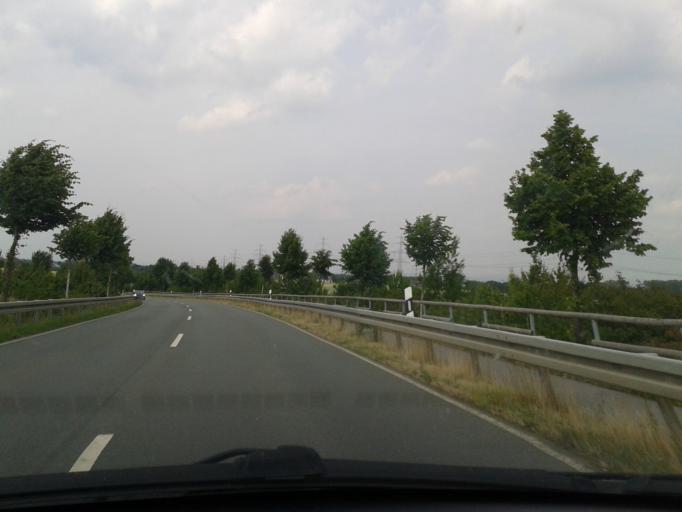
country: DE
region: North Rhine-Westphalia
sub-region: Regierungsbezirk Detmold
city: Paderborn
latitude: 51.7179
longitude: 8.6975
